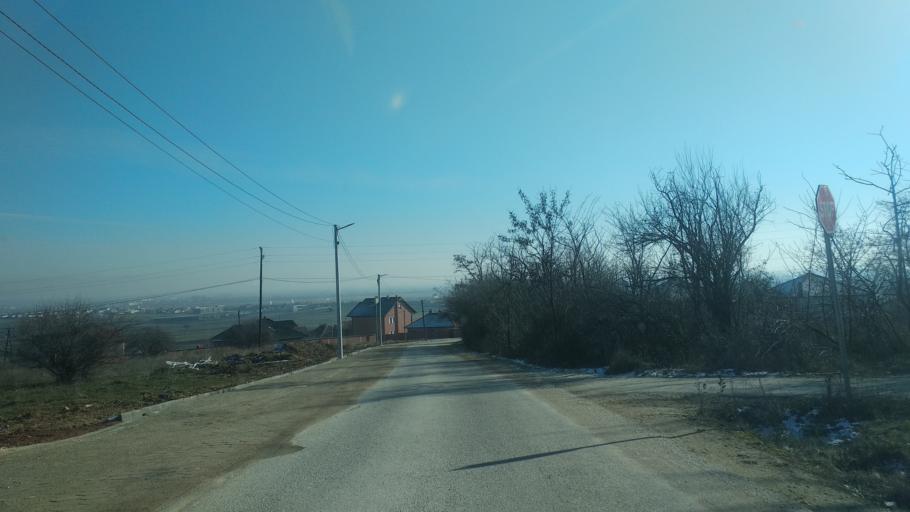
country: XK
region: Pristina
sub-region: Komuna e Gracanices
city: Glanica
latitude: 42.6074
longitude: 21.0261
